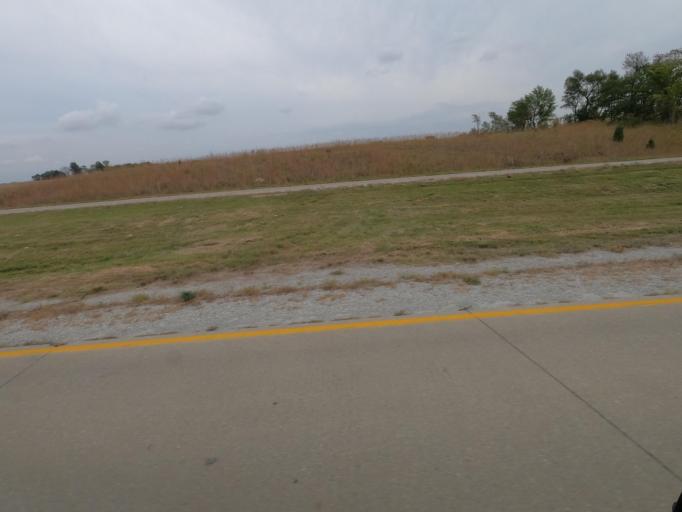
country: US
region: Iowa
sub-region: Jasper County
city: Monroe
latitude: 41.5194
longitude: -93.1304
